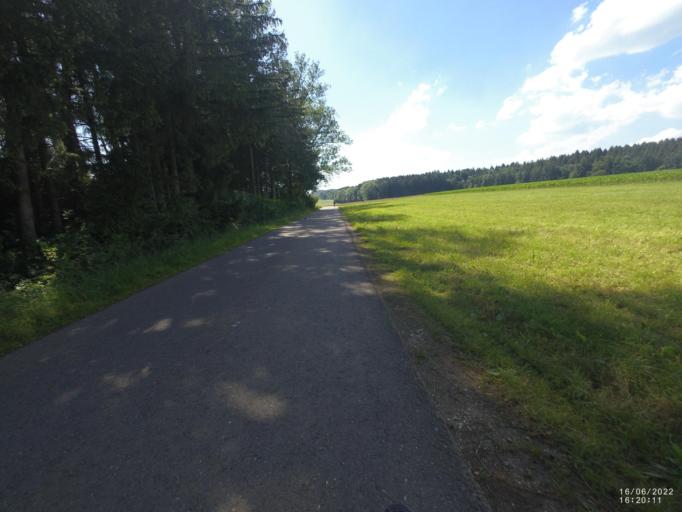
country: DE
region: Baden-Wuerttemberg
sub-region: Regierungsbezirk Stuttgart
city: Gerstetten
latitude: 48.6226
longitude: 10.0696
